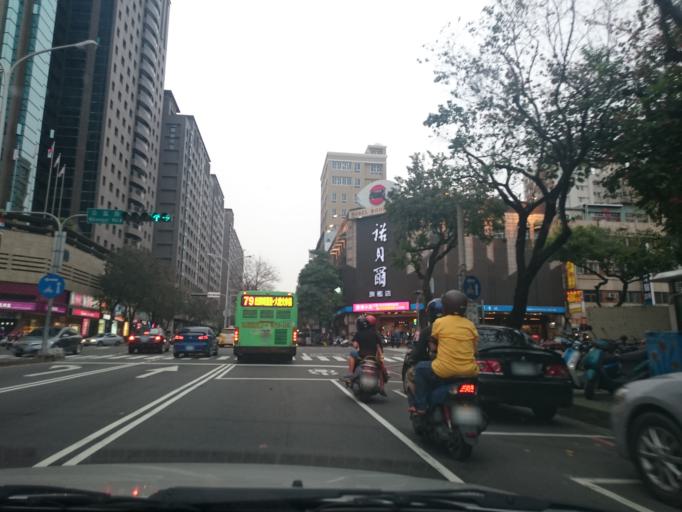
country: TW
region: Taiwan
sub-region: Taichung City
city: Taichung
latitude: 24.1505
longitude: 120.6574
